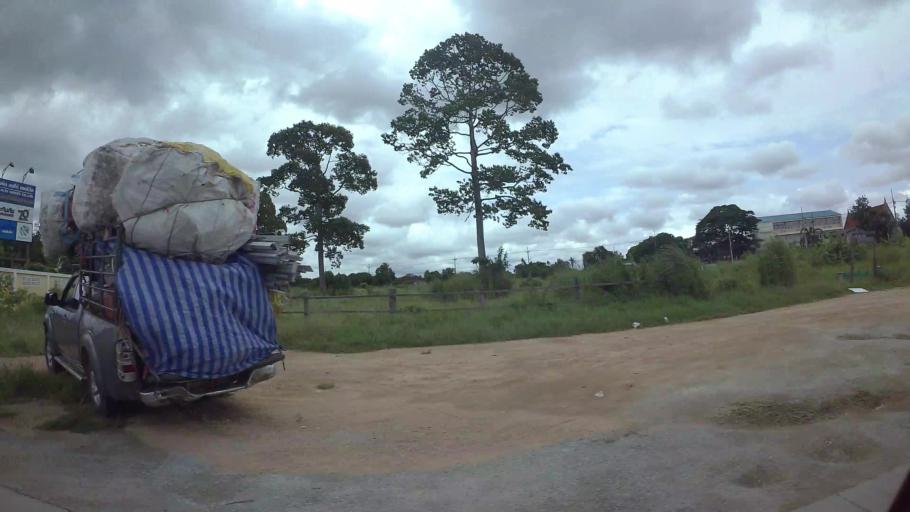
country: TH
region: Chon Buri
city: Si Racha
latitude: 13.1649
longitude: 100.9698
